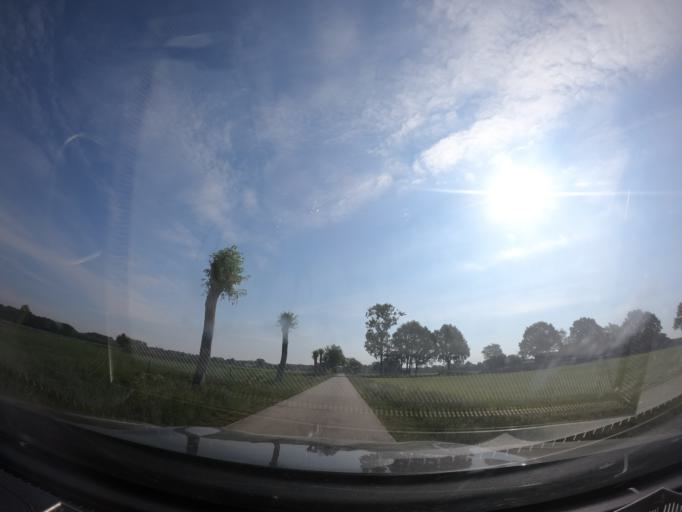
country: BE
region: Flanders
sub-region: Provincie Antwerpen
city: Olen
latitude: 51.1273
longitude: 4.8177
